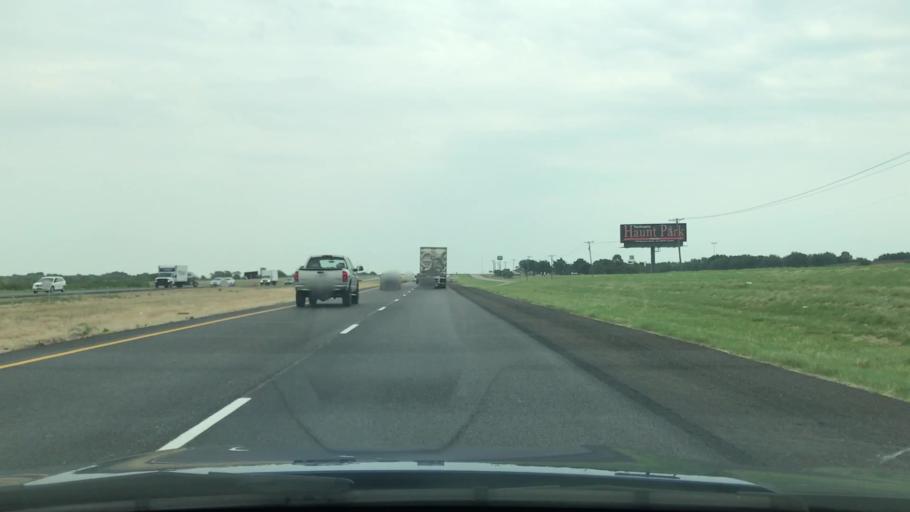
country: US
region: Texas
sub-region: Kaufman County
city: Terrell
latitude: 32.6952
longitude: -96.2530
